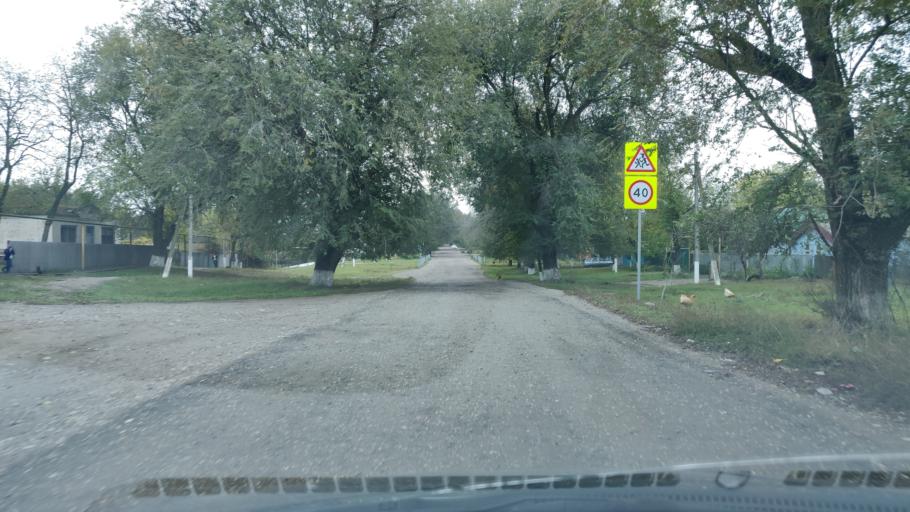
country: RU
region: Stavropol'skiy
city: Irgakly
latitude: 44.2454
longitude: 44.7195
